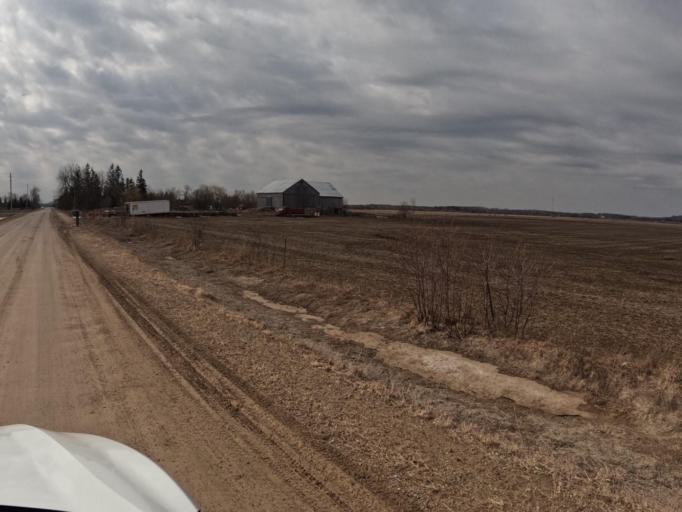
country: CA
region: Ontario
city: Orangeville
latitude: 43.9138
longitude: -80.2164
